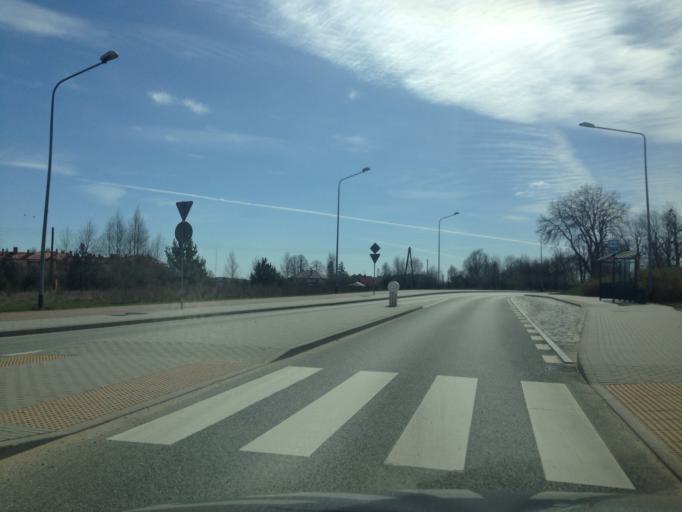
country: PL
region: Pomeranian Voivodeship
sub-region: Powiat wejherowski
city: Bojano
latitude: 54.4993
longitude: 18.4330
